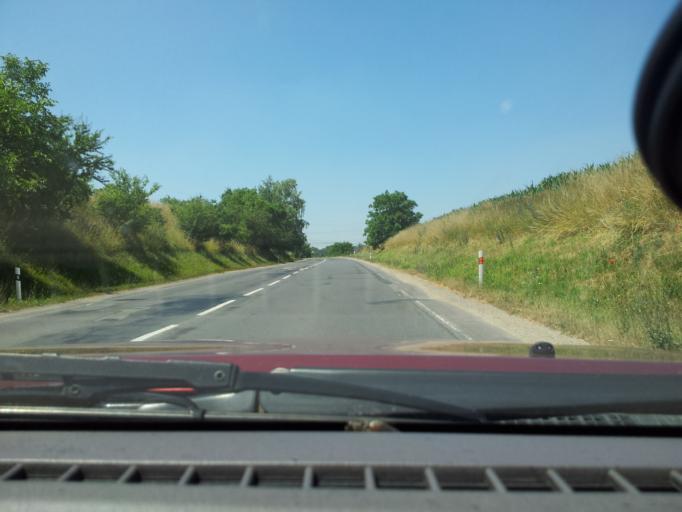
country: CZ
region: South Moravian
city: Krumvir
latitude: 48.9918
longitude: 16.9016
